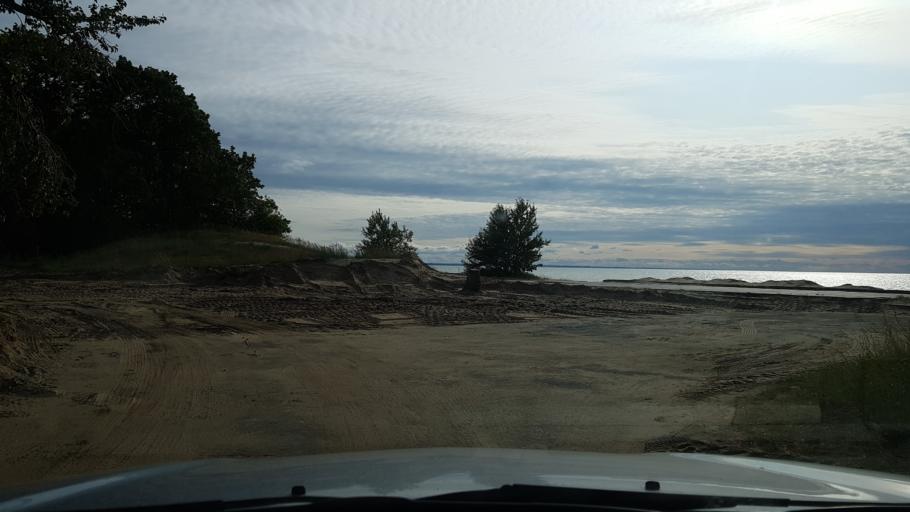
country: EE
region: Ida-Virumaa
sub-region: Narva-Joesuu linn
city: Narva-Joesuu
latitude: 59.4611
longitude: 28.0336
